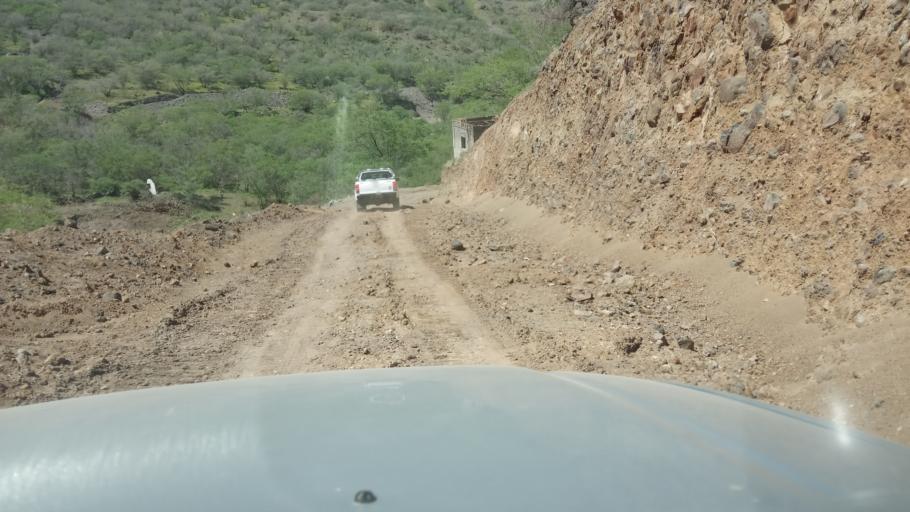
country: CV
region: Santa Catarina
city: Assomada
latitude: 15.1156
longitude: -23.7299
